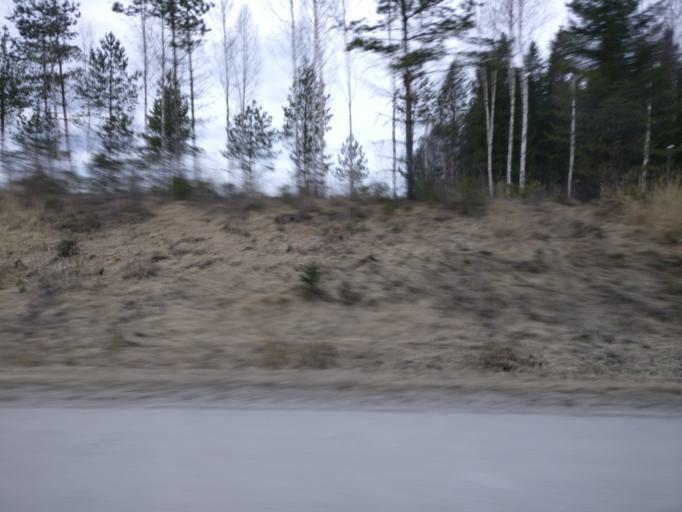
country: FI
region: Uusimaa
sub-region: Helsinki
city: Hyvinge
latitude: 60.5678
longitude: 24.8174
